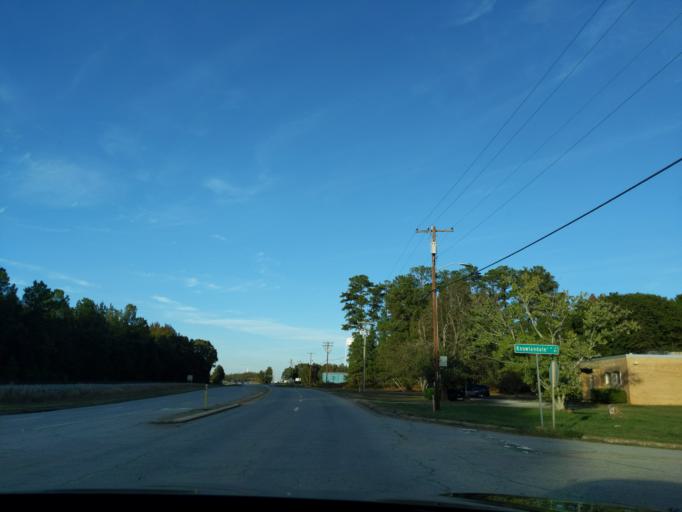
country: US
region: South Carolina
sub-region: Anderson County
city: Homeland Park
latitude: 34.4272
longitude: -82.6648
